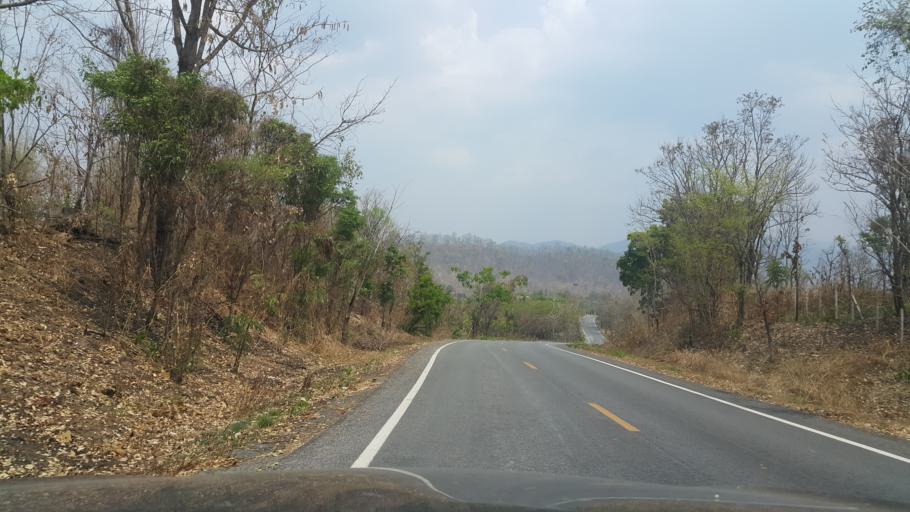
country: TH
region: Lamphun
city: Ban Hong
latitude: 18.2651
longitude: 98.9231
